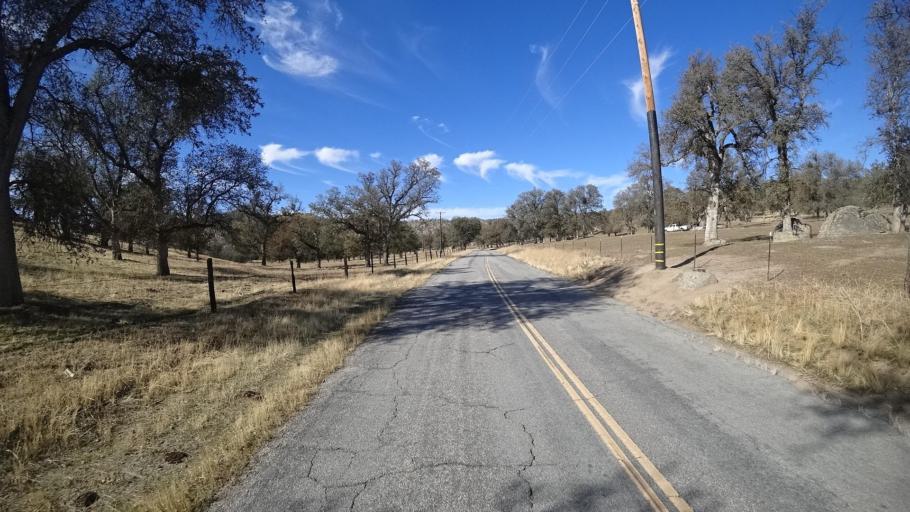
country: US
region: California
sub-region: Kern County
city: Alta Sierra
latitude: 35.6213
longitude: -118.7392
